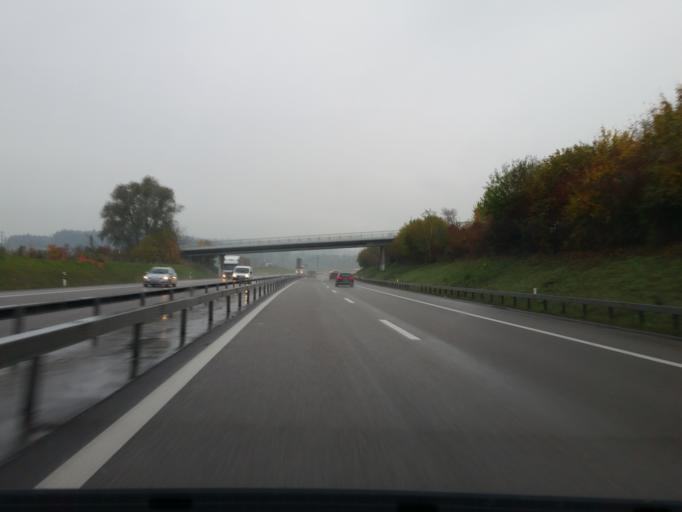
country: CH
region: Thurgau
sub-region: Frauenfeld District
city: Gachnang
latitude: 47.5473
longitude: 8.8237
